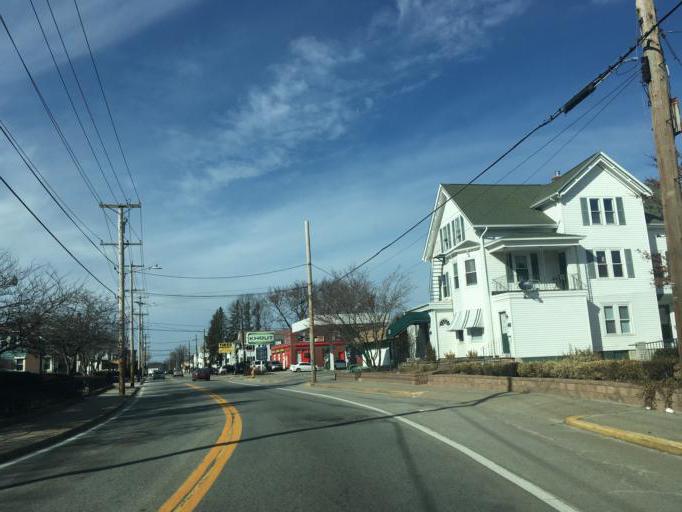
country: US
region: Rhode Island
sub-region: Providence County
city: Central Falls
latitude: 41.8919
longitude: -71.4026
